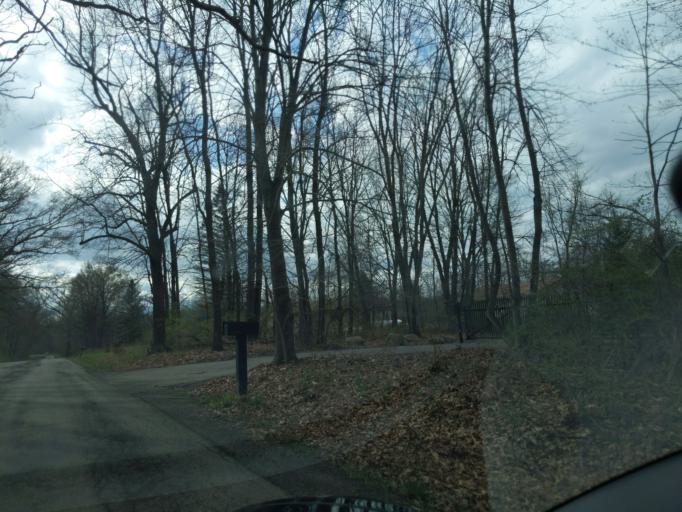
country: US
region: Michigan
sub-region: Jackson County
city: Jackson
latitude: 42.3421
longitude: -84.3891
